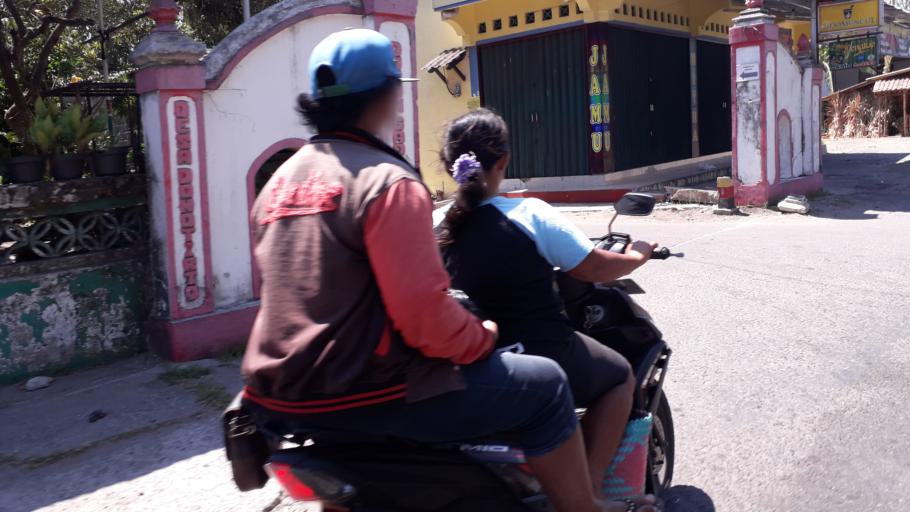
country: ID
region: Daerah Istimewa Yogyakarta
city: Pundong
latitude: -7.9860
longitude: 110.3157
